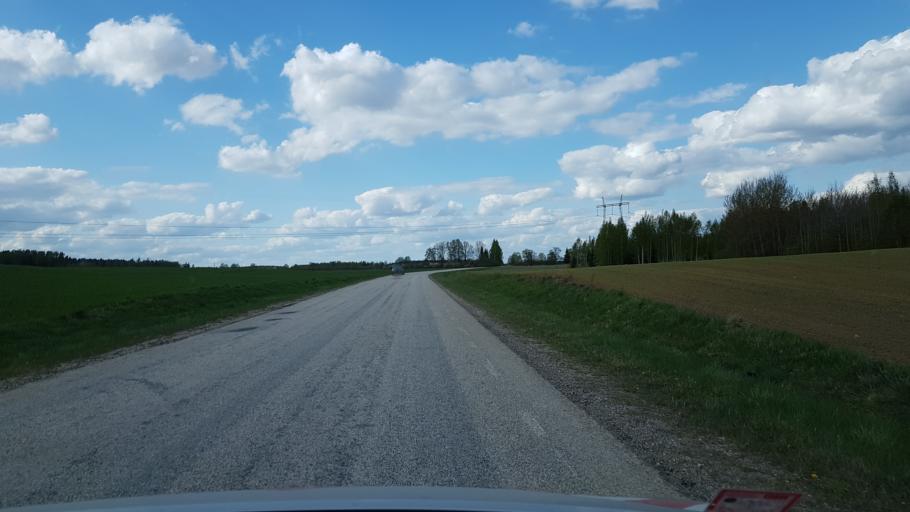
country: EE
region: Tartu
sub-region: UElenurme vald
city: Ulenurme
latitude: 58.2724
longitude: 26.9078
